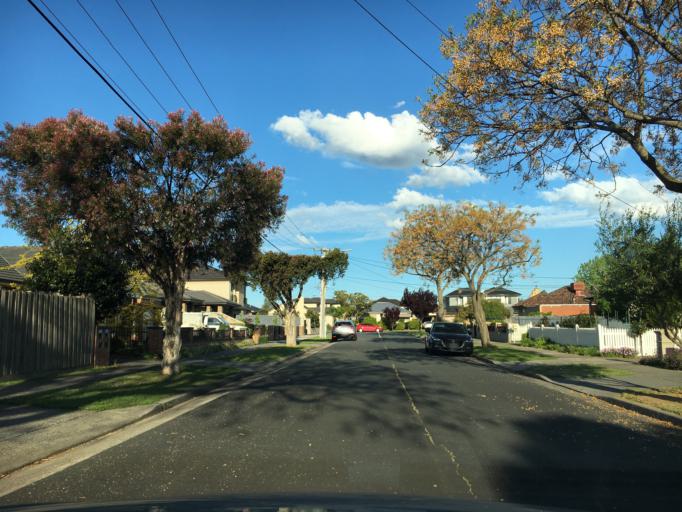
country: AU
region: Victoria
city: Clayton
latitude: -37.9038
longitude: 145.1180
